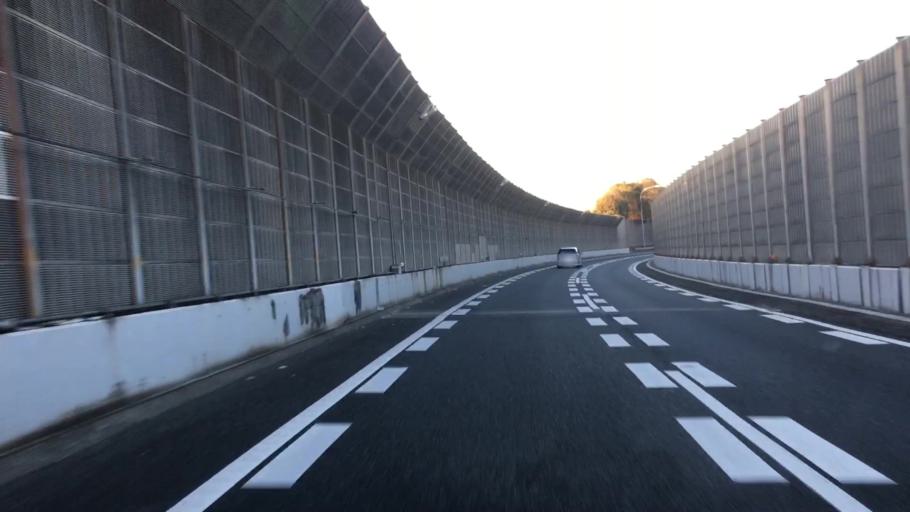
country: JP
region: Kanagawa
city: Yokohama
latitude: 35.4078
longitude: 139.5746
